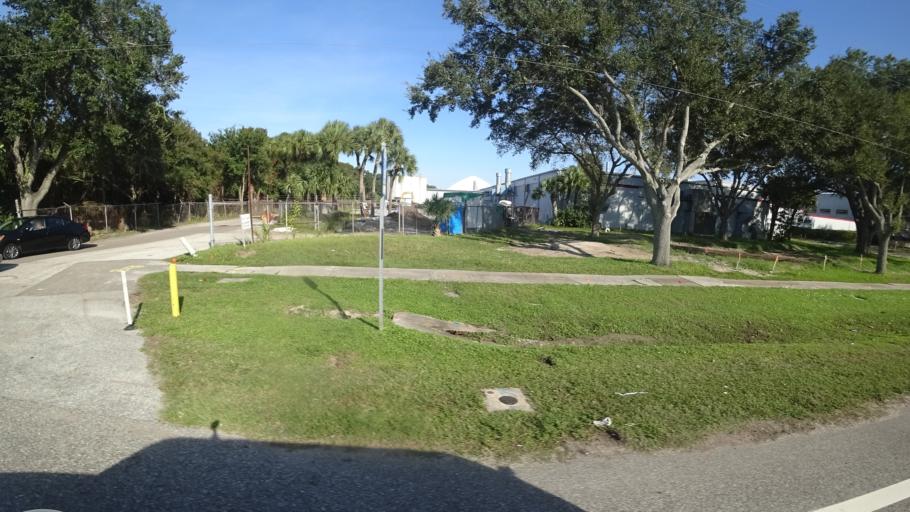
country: US
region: Florida
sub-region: Manatee County
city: Whitfield
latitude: 27.3960
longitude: -82.5468
